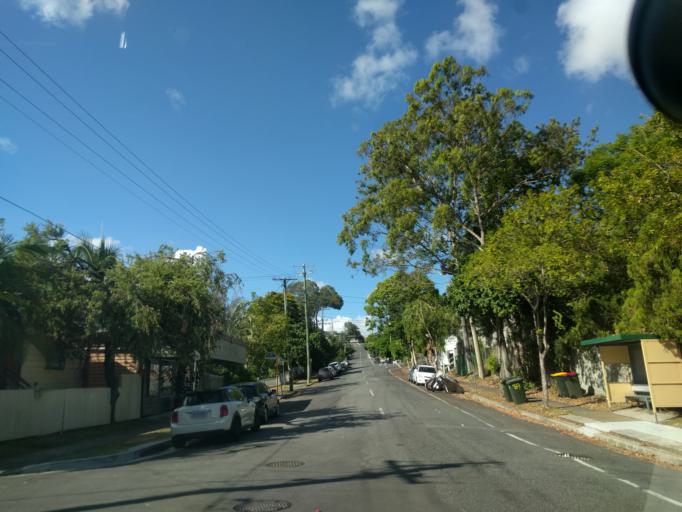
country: AU
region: Queensland
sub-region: Brisbane
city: Milton
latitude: -27.4562
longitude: 153.0040
